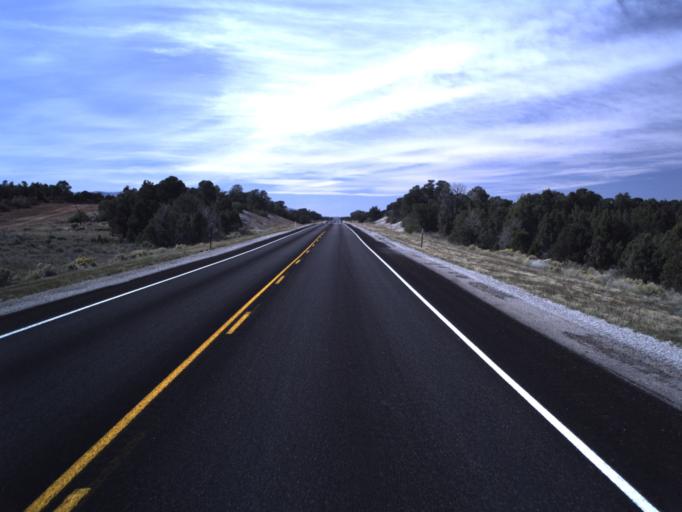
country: US
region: Colorado
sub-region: Dolores County
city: Dove Creek
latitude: 37.8280
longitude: -109.0818
